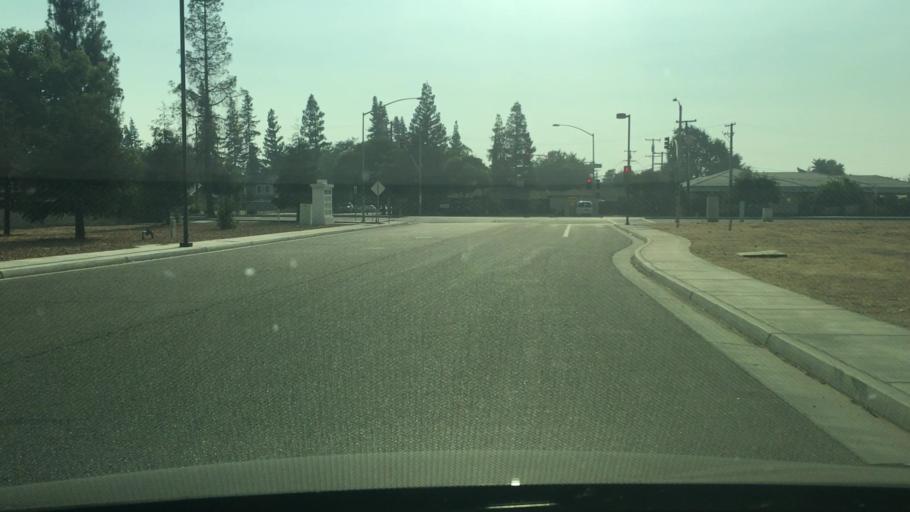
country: US
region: California
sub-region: Fresno County
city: Clovis
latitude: 36.8359
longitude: -119.7803
